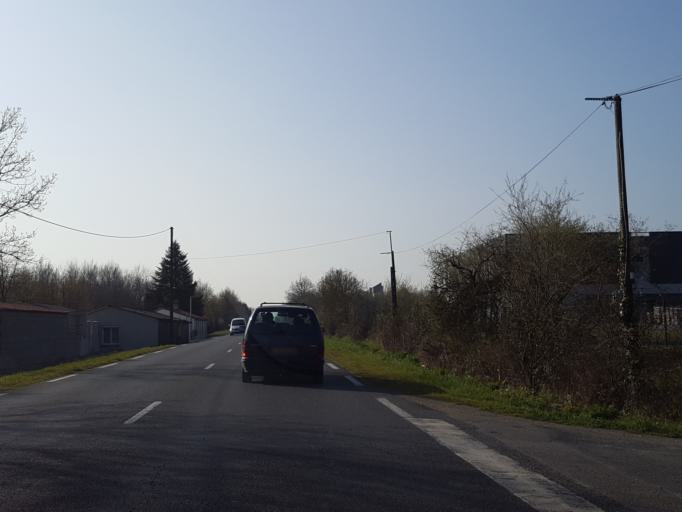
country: FR
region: Pays de la Loire
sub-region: Departement de la Loire-Atlantique
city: Geneston
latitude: 47.0880
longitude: -1.5283
